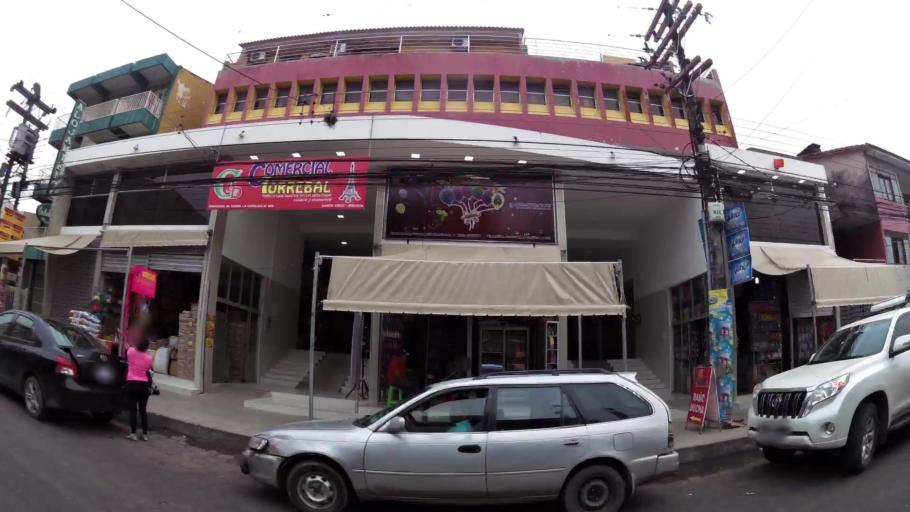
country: BO
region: Santa Cruz
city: Santa Cruz de la Sierra
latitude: -17.7948
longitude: -63.1924
